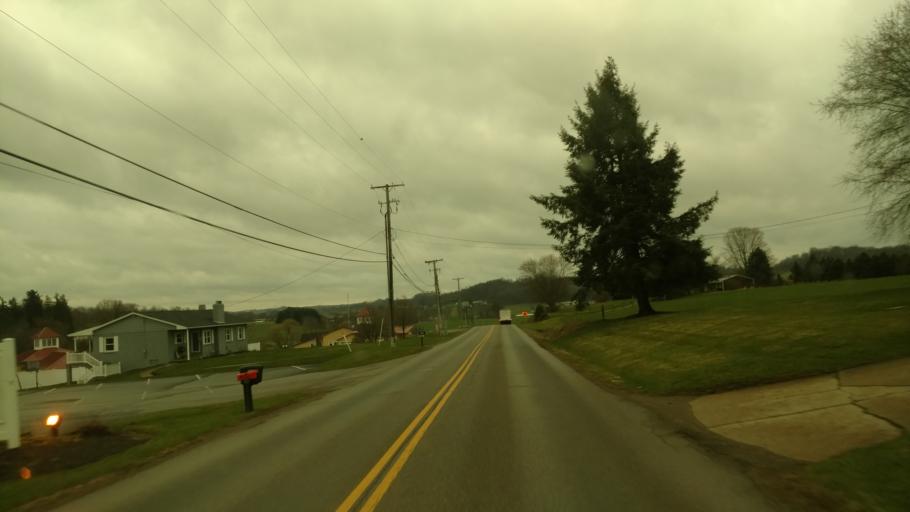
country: US
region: Ohio
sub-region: Holmes County
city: Millersburg
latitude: 40.5580
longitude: -81.8209
